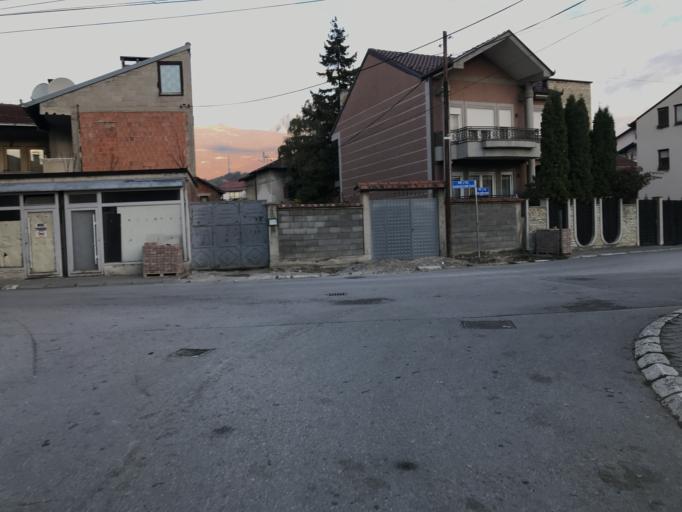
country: XK
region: Pec
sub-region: Komuna e Pejes
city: Peje
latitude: 42.6594
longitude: 20.2986
